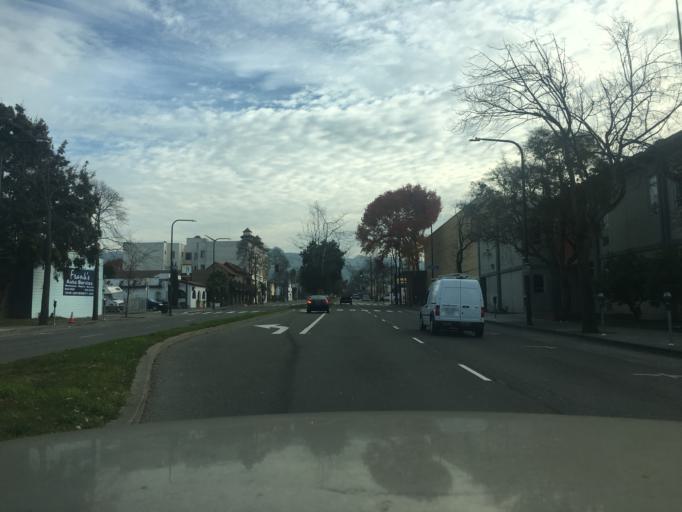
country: US
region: California
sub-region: Alameda County
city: Berkeley
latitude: 37.8695
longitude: -122.2890
